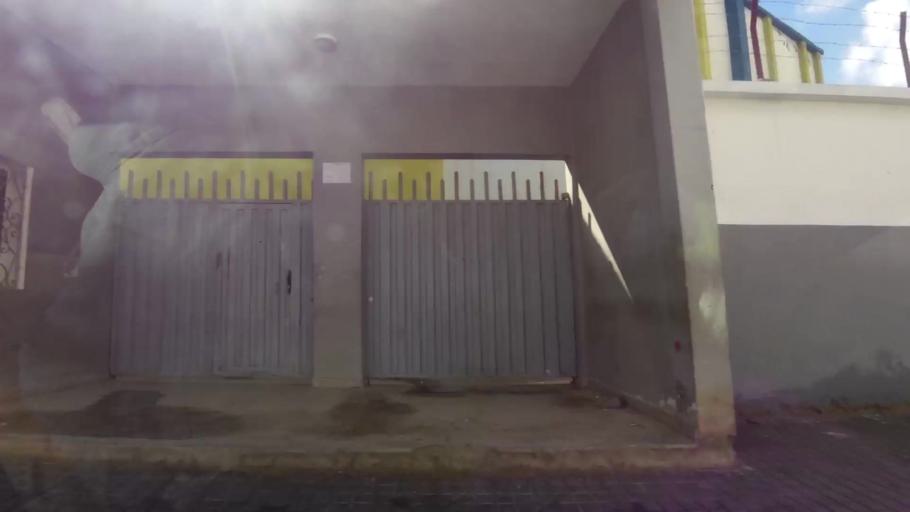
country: MA
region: Grand Casablanca
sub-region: Nouaceur
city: Bouskoura
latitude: 33.5295
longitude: -7.6716
